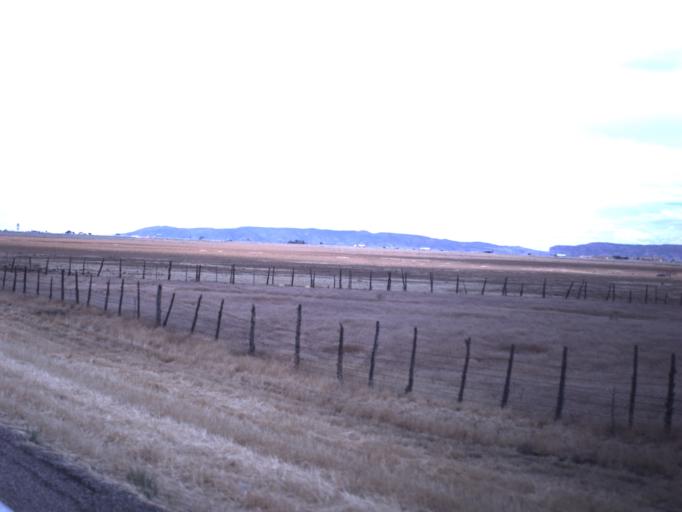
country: US
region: Utah
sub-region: Iron County
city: Parowan
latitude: 37.8694
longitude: -112.7967
